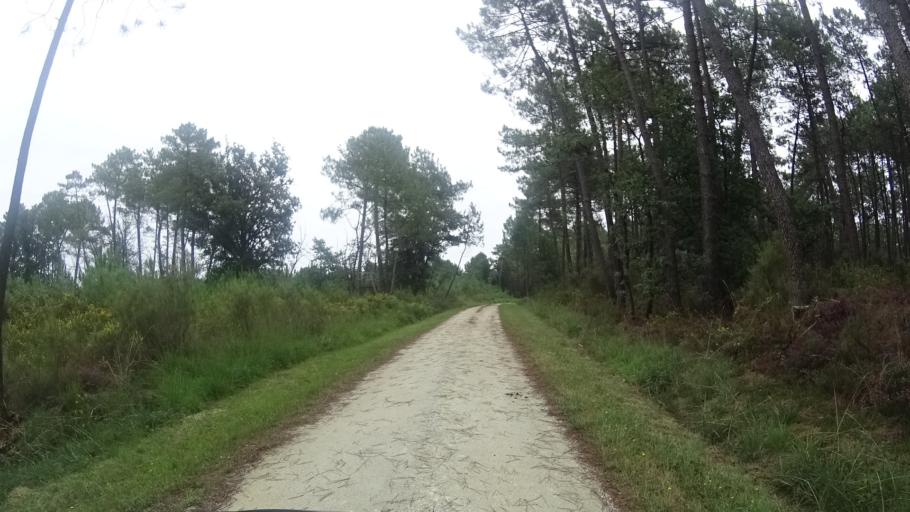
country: FR
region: Aquitaine
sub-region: Departement de la Dordogne
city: Sourzac
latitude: 45.0357
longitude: 0.4532
